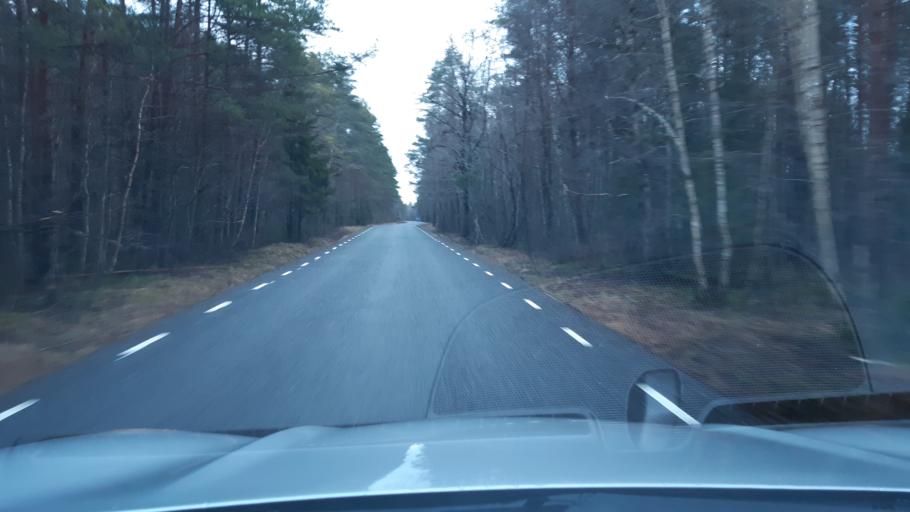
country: EE
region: Harju
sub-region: Saku vald
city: Saku
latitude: 59.1940
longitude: 24.6004
